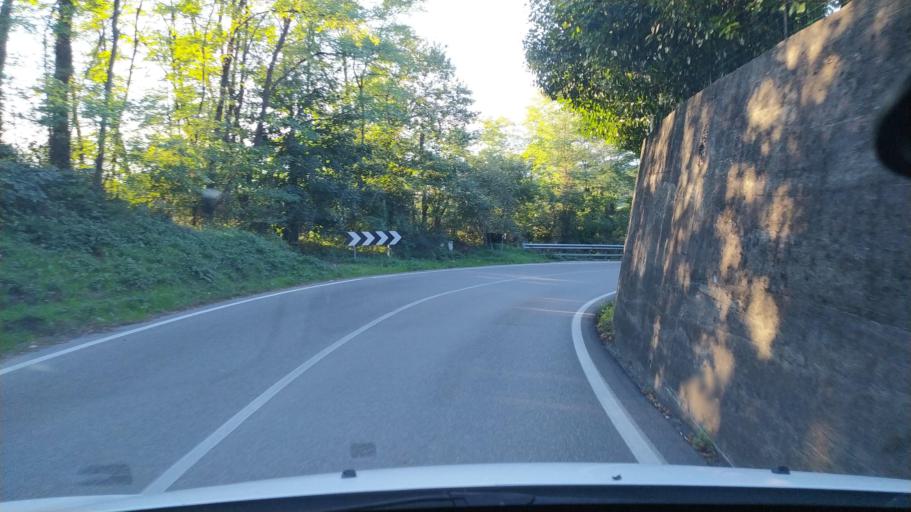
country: IT
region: Lombardy
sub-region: Provincia di Varese
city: Golasecca
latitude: 45.7040
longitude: 8.6565
